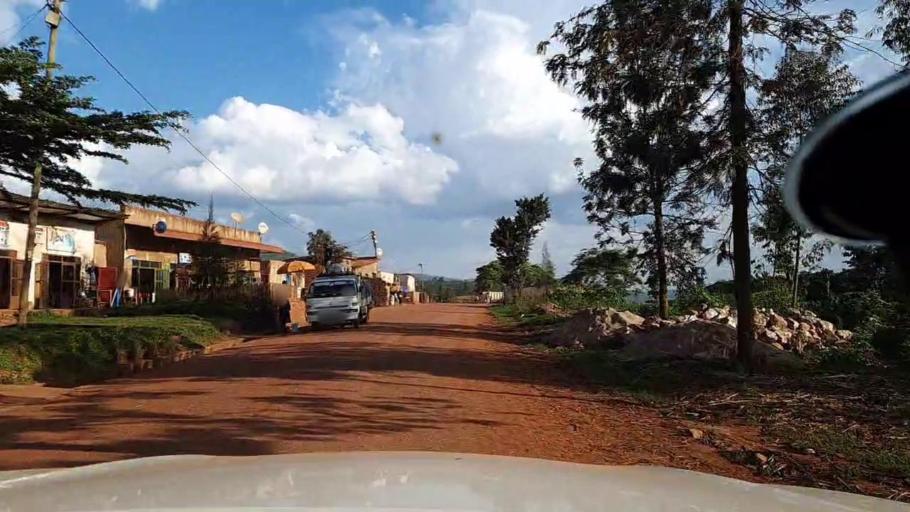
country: RW
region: Kigali
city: Kigali
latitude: -1.9101
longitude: 29.9822
